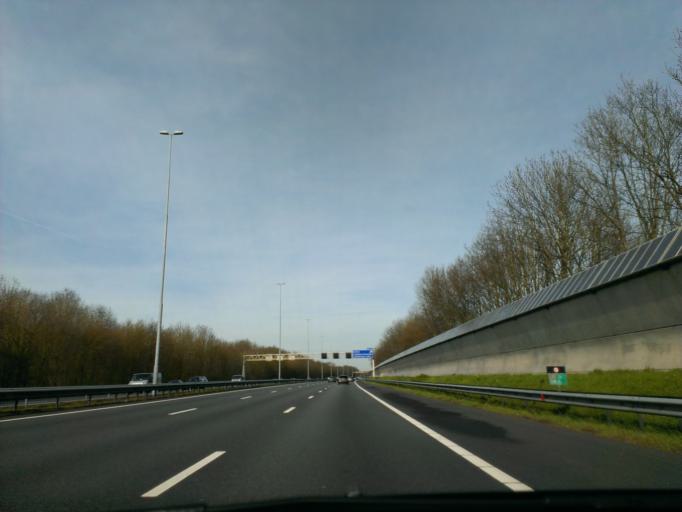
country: NL
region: North Holland
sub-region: Gemeente Ouder-Amstel
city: Ouderkerk aan de Amstel
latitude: 52.2892
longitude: 4.9116
